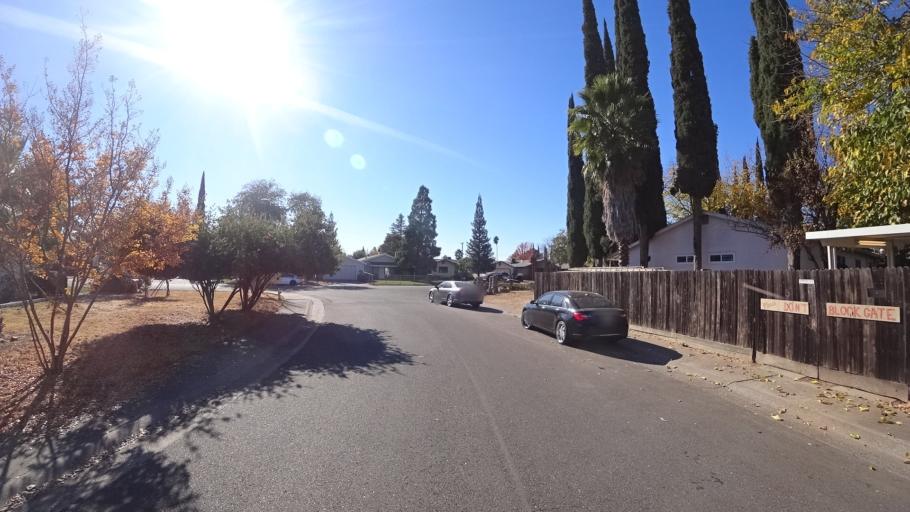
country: US
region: California
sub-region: Sacramento County
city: Antelope
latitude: 38.7154
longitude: -121.3127
